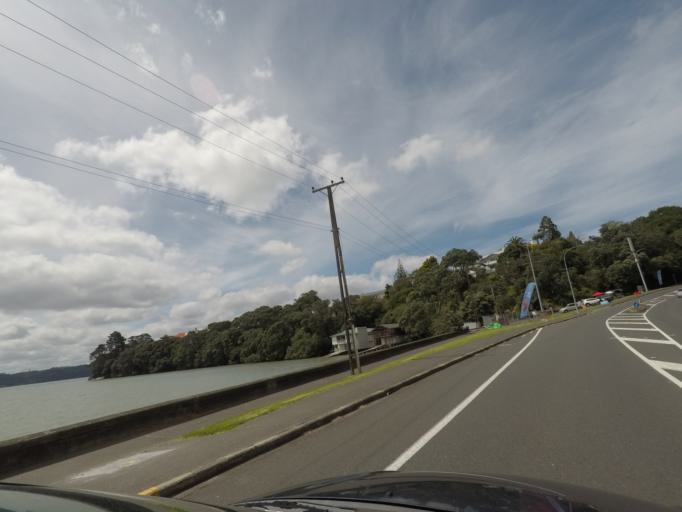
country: NZ
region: Auckland
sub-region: Auckland
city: Auckland
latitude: -36.8511
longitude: 174.7246
